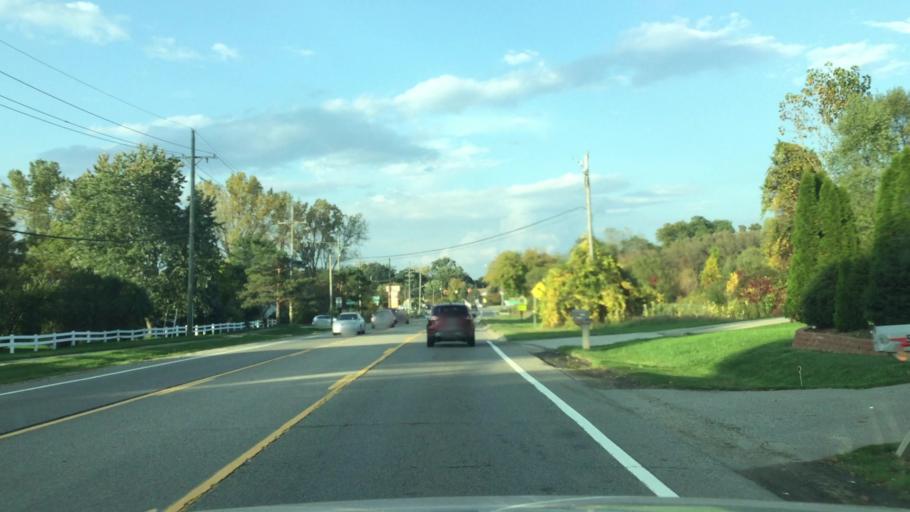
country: US
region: Michigan
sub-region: Oakland County
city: Keego Harbor
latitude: 42.6256
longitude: -83.3961
